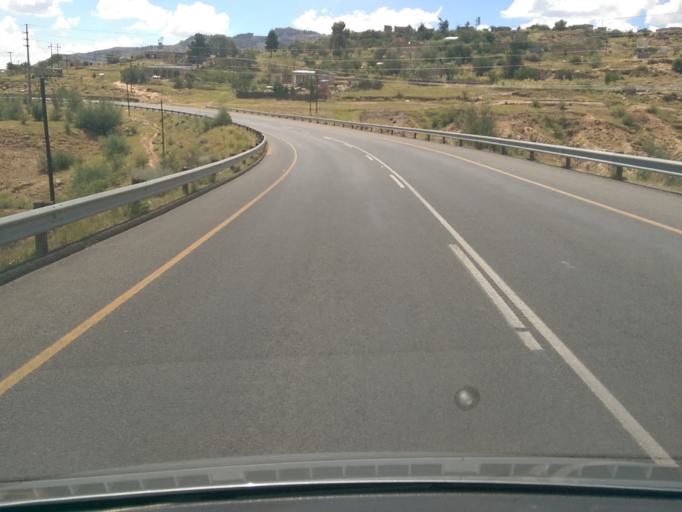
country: LS
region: Maseru
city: Maseru
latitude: -29.3777
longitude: 27.4955
